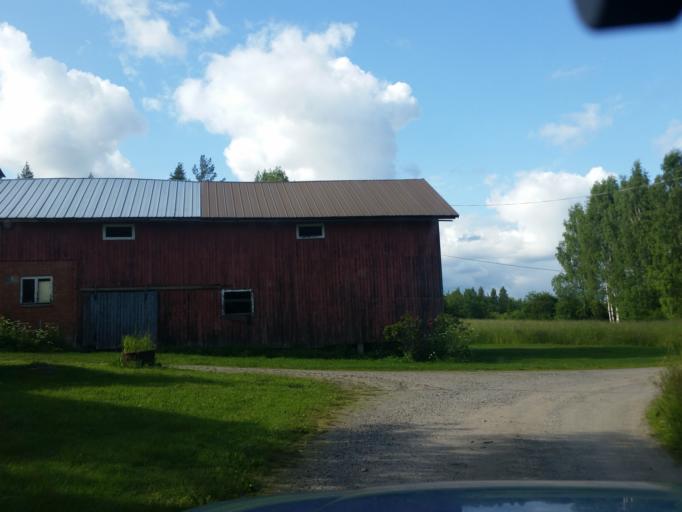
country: FI
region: Southern Savonia
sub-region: Savonlinna
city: Sulkava
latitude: 61.6767
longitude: 28.2823
